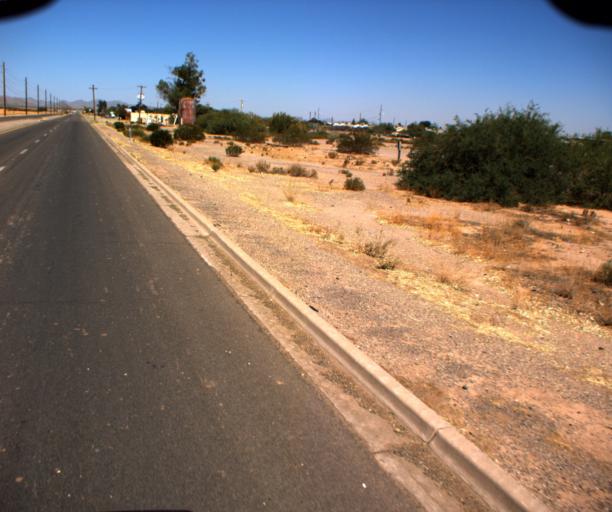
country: US
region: Arizona
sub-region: Pinal County
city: Maricopa
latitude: 32.8795
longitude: -111.9707
